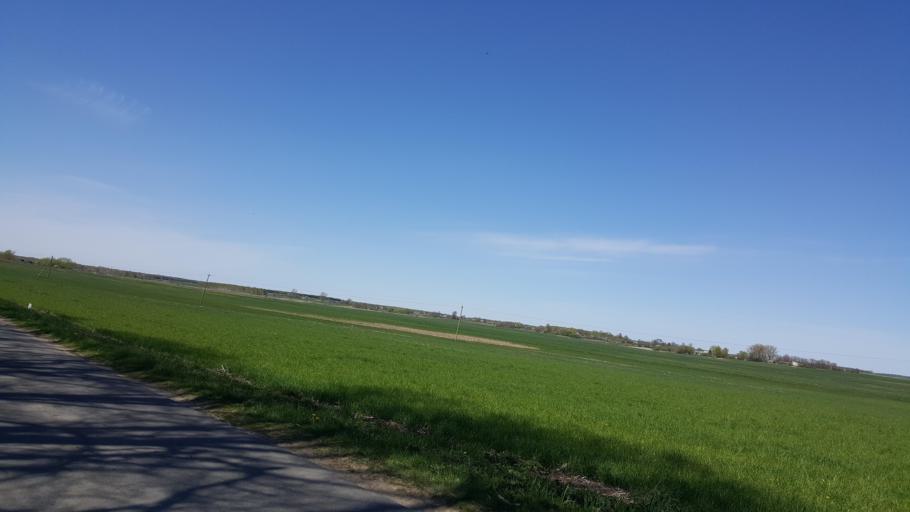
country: BY
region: Brest
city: Vysokaye
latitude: 52.3481
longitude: 23.5313
